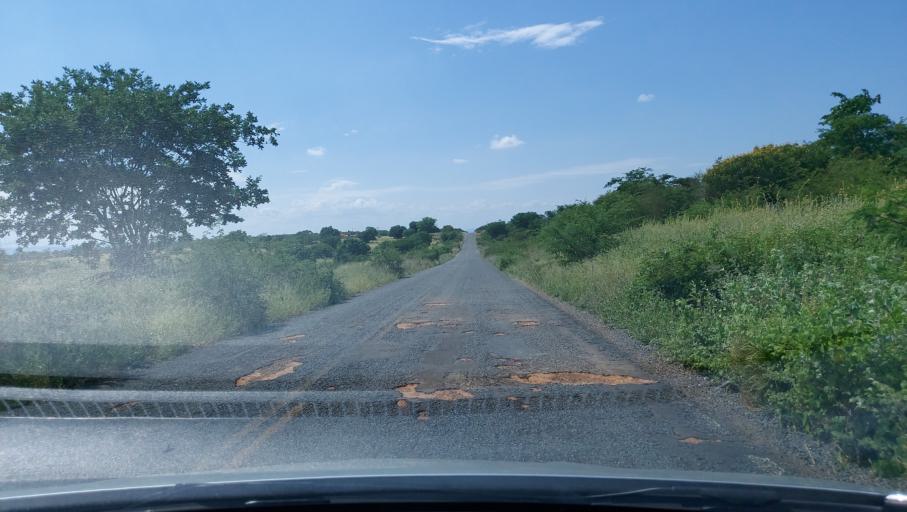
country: BR
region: Bahia
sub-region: Oliveira Dos Brejinhos
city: Beira Rio
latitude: -12.1582
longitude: -42.5506
